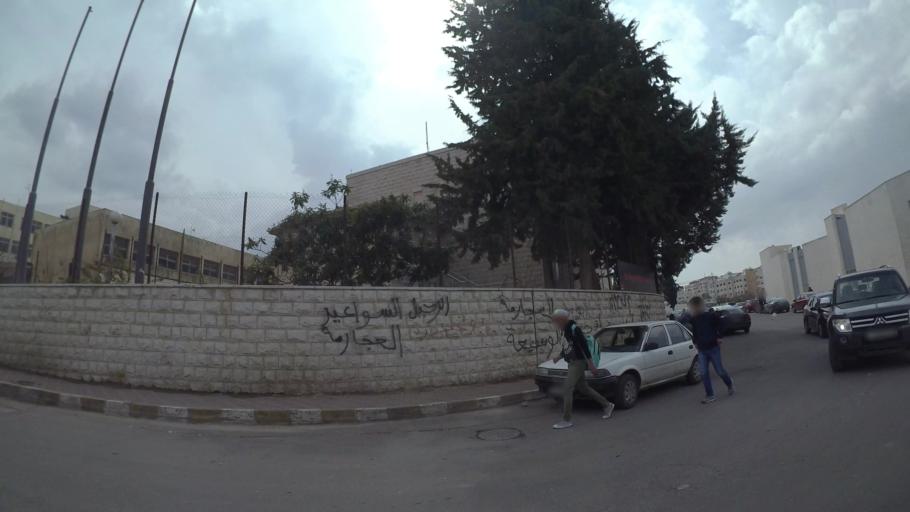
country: JO
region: Amman
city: Umm as Summaq
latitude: 31.8908
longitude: 35.8457
